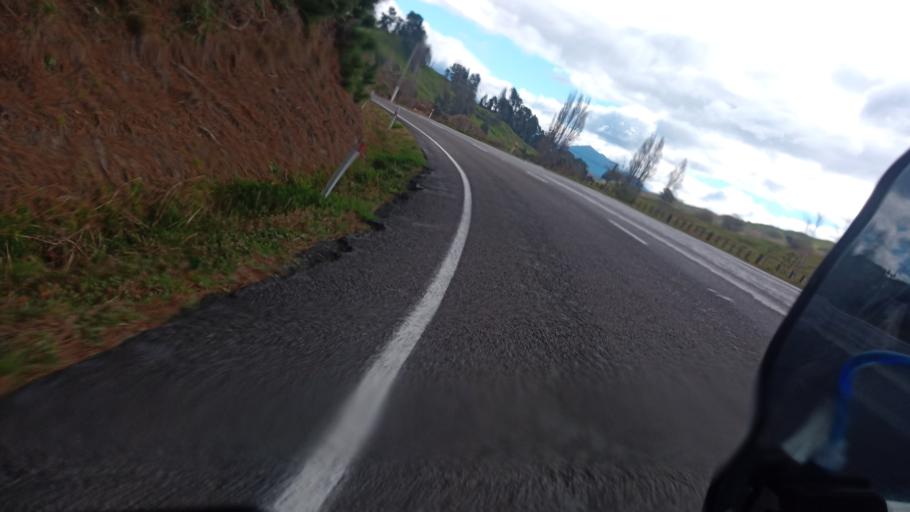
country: NZ
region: Gisborne
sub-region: Gisborne District
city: Gisborne
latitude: -38.0377
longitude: 178.2923
